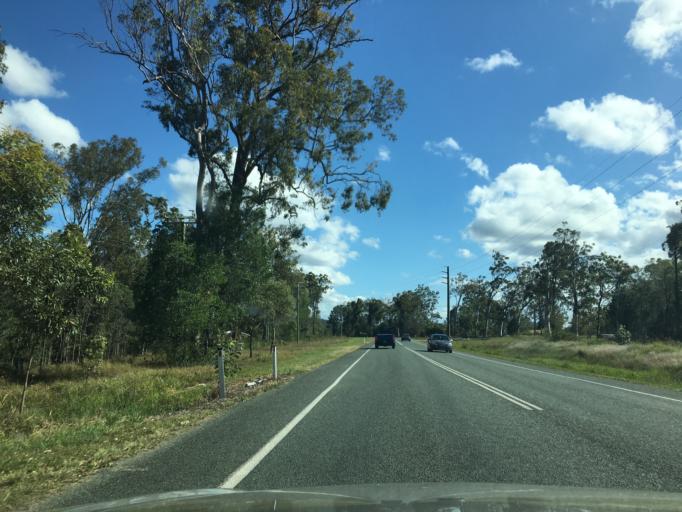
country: AU
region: Queensland
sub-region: Logan
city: Chambers Flat
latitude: -27.7806
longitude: 153.1001
